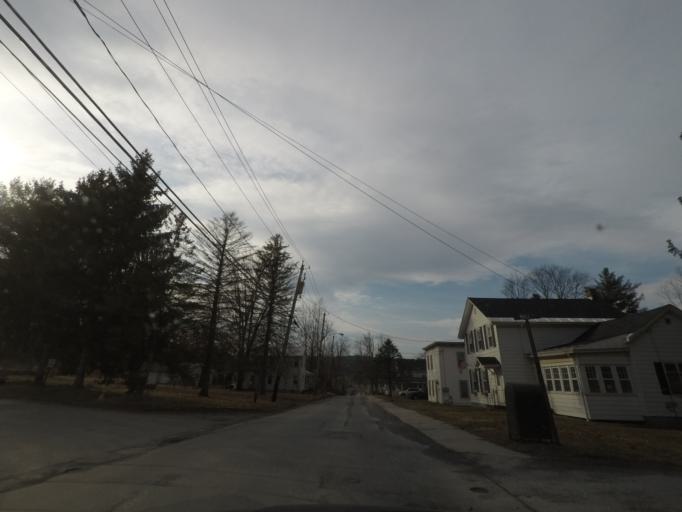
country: US
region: New York
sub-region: Rensselaer County
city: Hoosick Falls
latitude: 42.9061
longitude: -73.3559
